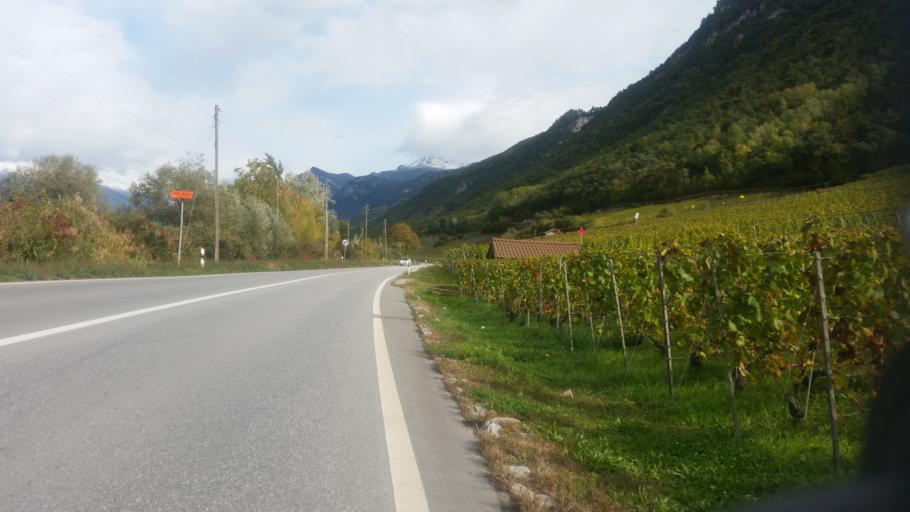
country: CH
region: Valais
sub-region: Sion District
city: Saint-Leonard
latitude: 46.2456
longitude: 7.4348
